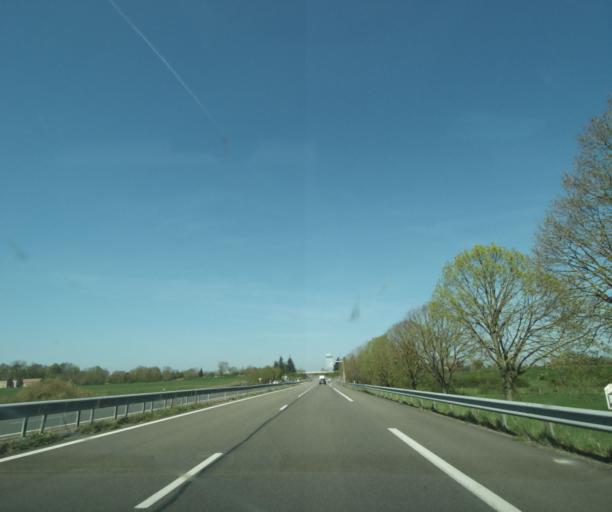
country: FR
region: Bourgogne
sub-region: Departement de la Nievre
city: La Charite-sur-Loire
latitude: 47.1814
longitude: 3.0400
